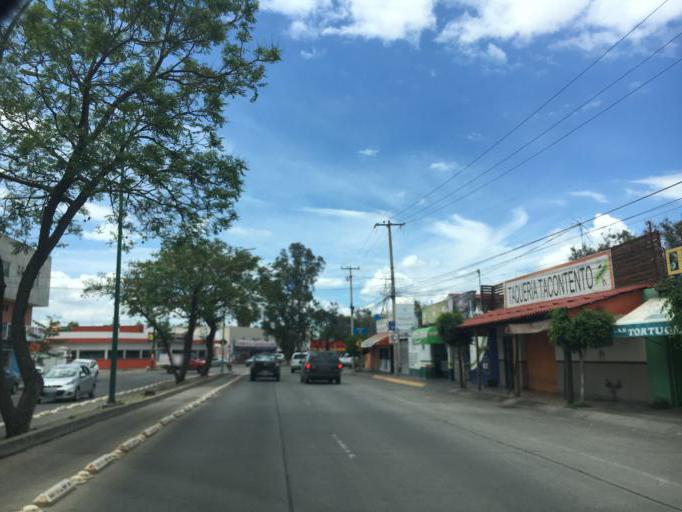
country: MX
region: Guanajuato
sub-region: Leon
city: Medina
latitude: 21.1113
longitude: -101.6350
